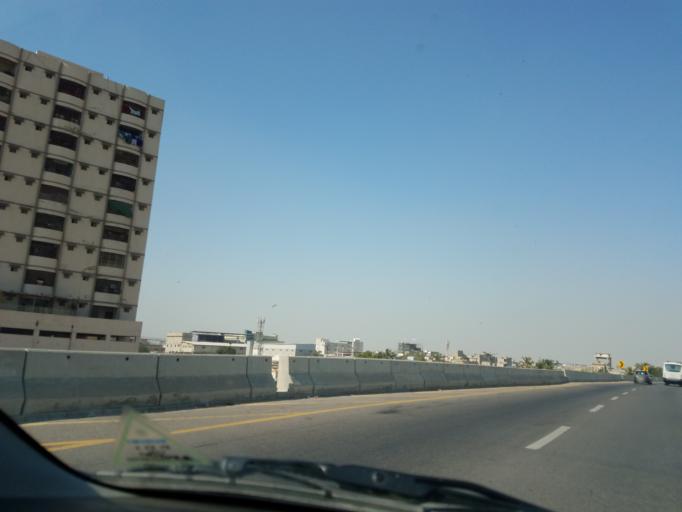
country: PK
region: Sindh
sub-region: Karachi District
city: Karachi
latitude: 24.9066
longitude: 67.0634
